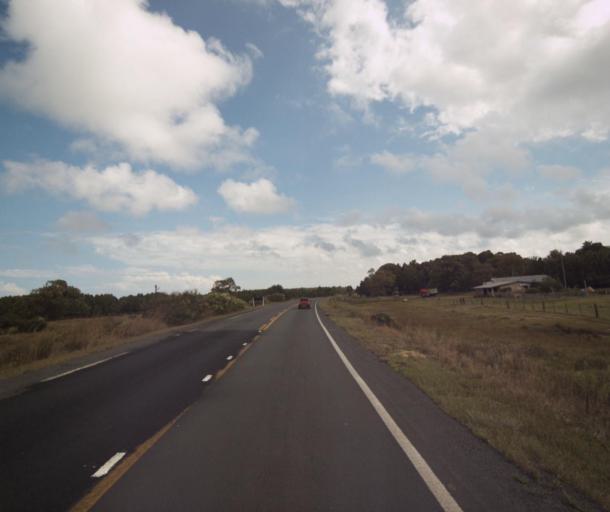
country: BR
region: Rio Grande do Sul
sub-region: Tapes
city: Tapes
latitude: -31.4105
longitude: -51.1688
